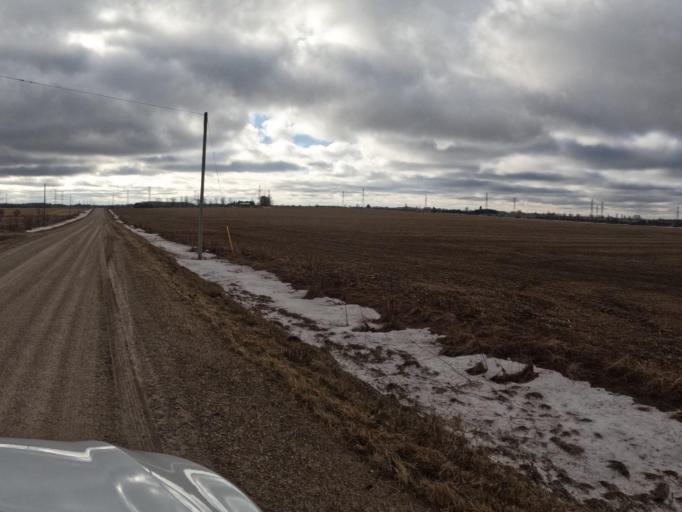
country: CA
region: Ontario
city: Shelburne
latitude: 44.0009
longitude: -80.3872
